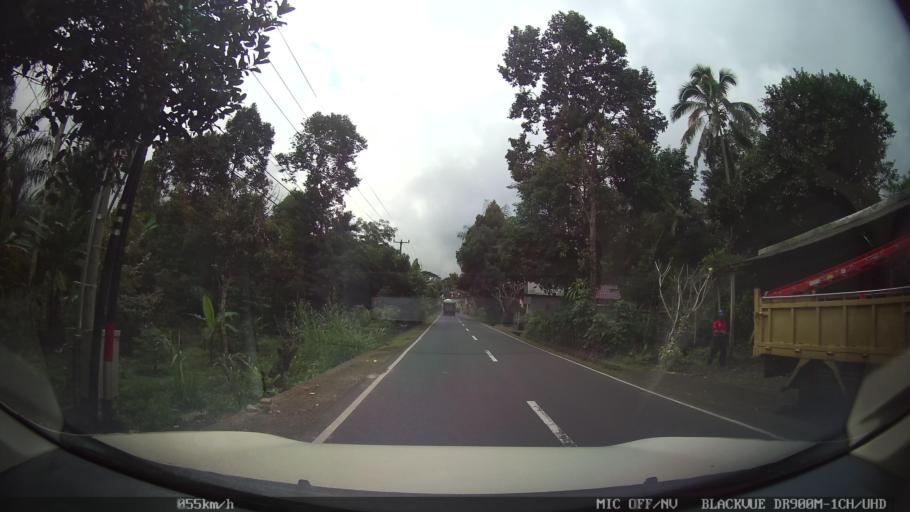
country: ID
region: Bali
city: Banjar Tiga
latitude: -8.3886
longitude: 115.4185
